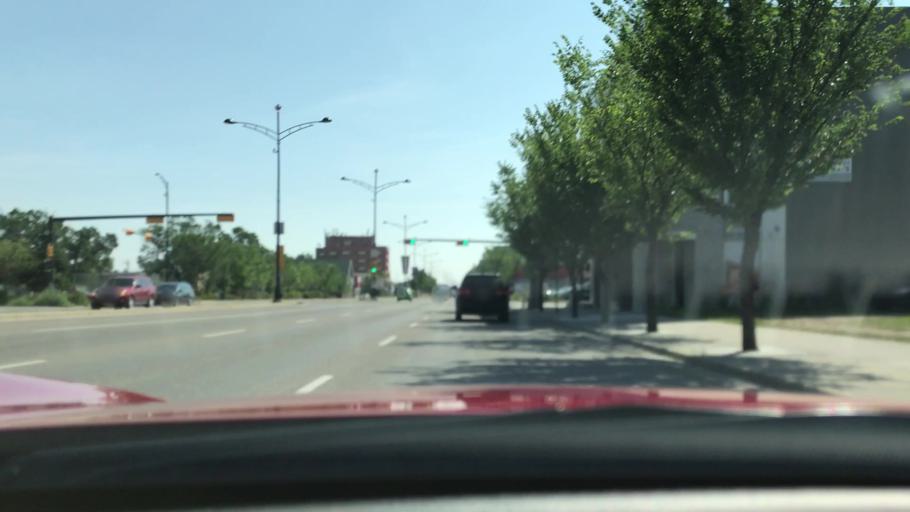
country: CA
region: Alberta
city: Calgary
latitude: 51.0668
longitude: -114.0685
